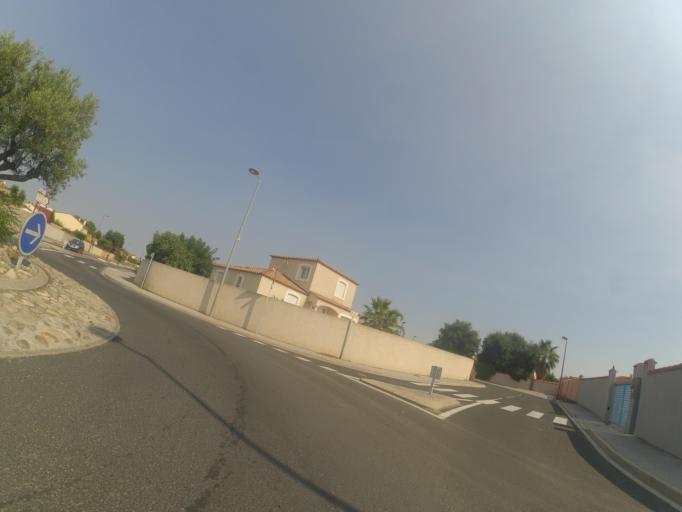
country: FR
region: Languedoc-Roussillon
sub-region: Departement des Pyrenees-Orientales
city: Toulouges
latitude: 42.6673
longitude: 2.8384
